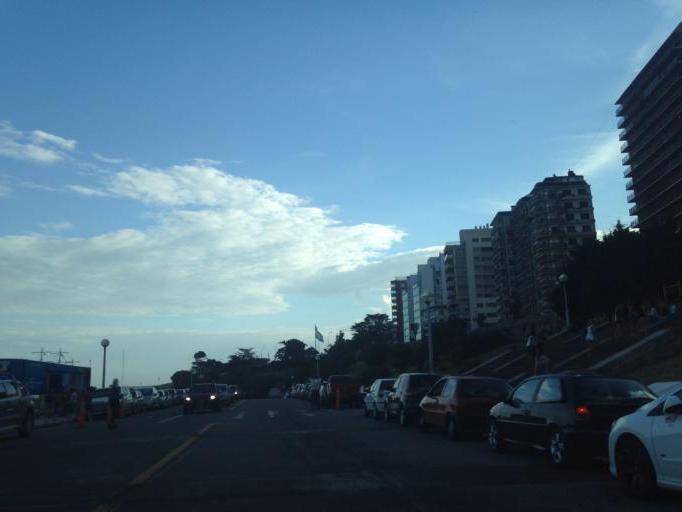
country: AR
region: Buenos Aires
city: Mar del Plata
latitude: -38.0278
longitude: -57.5331
